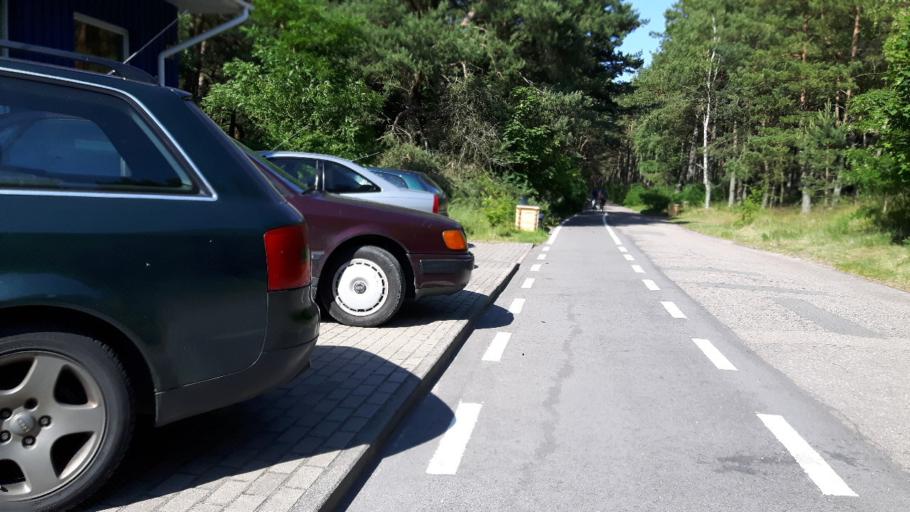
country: LT
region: Klaipedos apskritis
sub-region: Klaipeda
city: Klaipeda
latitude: 55.6991
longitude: 21.1034
